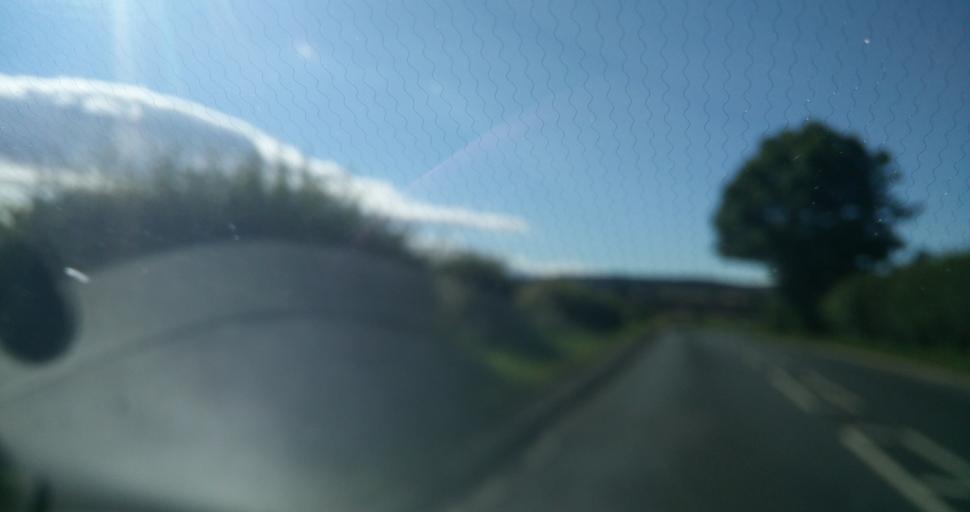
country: GB
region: England
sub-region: County Durham
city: Spennymoor
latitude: 54.7419
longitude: -1.6113
